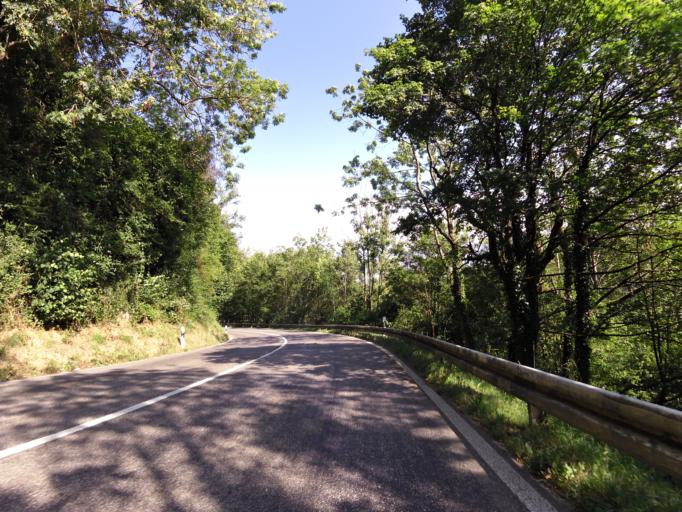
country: CH
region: Solothurn
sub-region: Bezirk Goesgen
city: Trimbach
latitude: 47.3692
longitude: 7.8798
